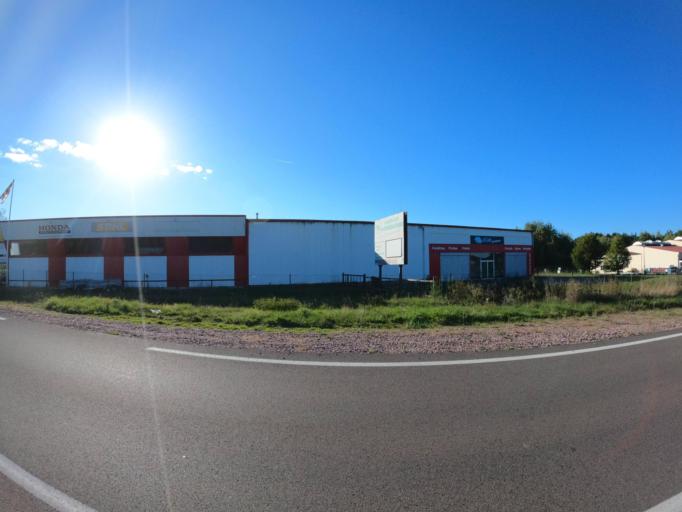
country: FR
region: Bourgogne
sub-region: Departement de Saone-et-Loire
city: Blanzy
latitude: 46.7046
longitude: 4.4113
